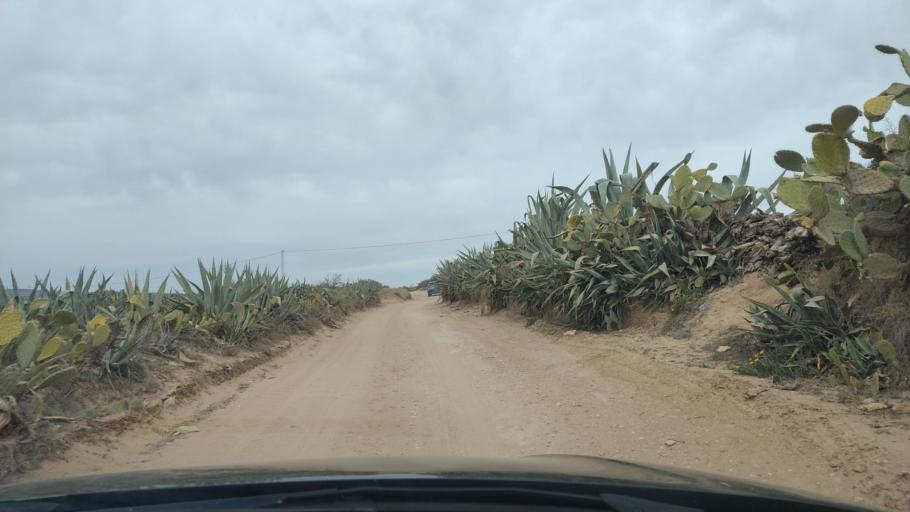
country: TN
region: Al Qasrayn
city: Kasserine
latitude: 35.2468
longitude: 8.9194
